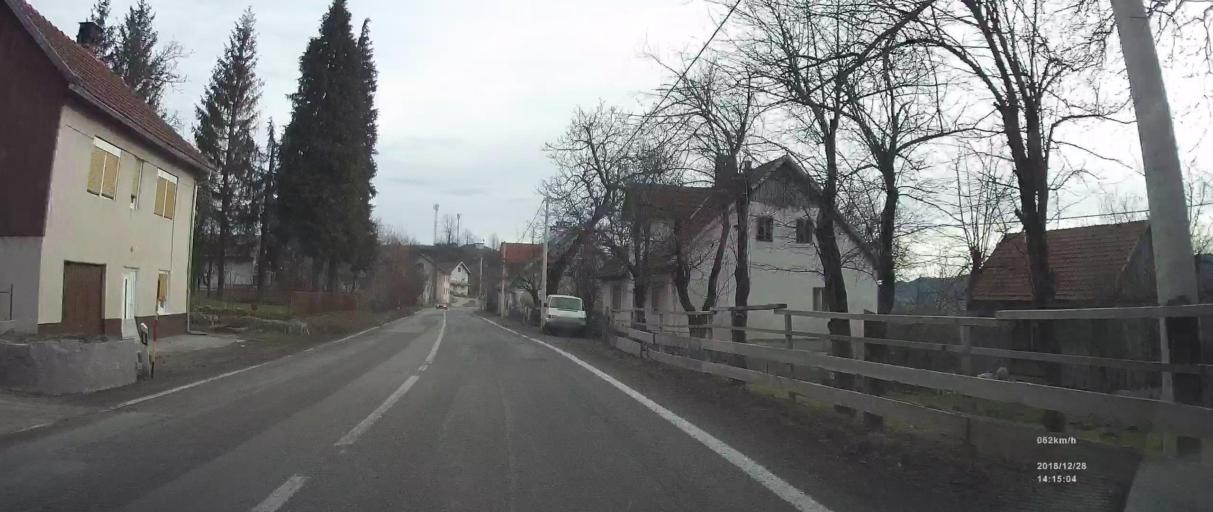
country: HR
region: Primorsko-Goranska
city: Vrbovsko
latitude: 45.4272
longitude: 15.0246
